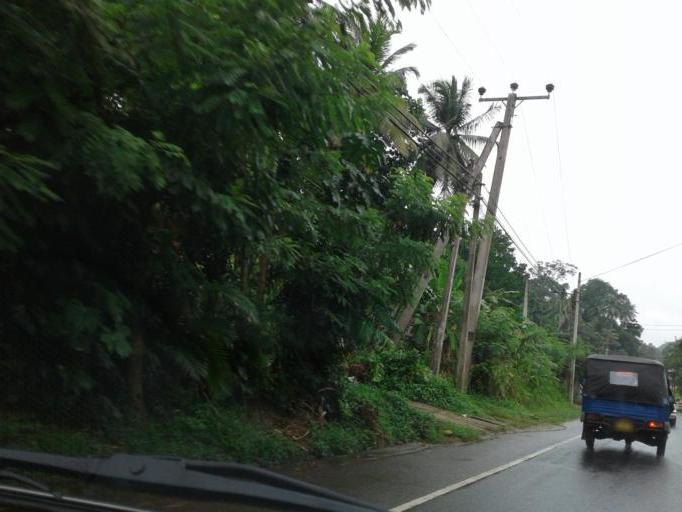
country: LK
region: Central
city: Kadugannawa
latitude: 7.2399
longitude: 80.3219
